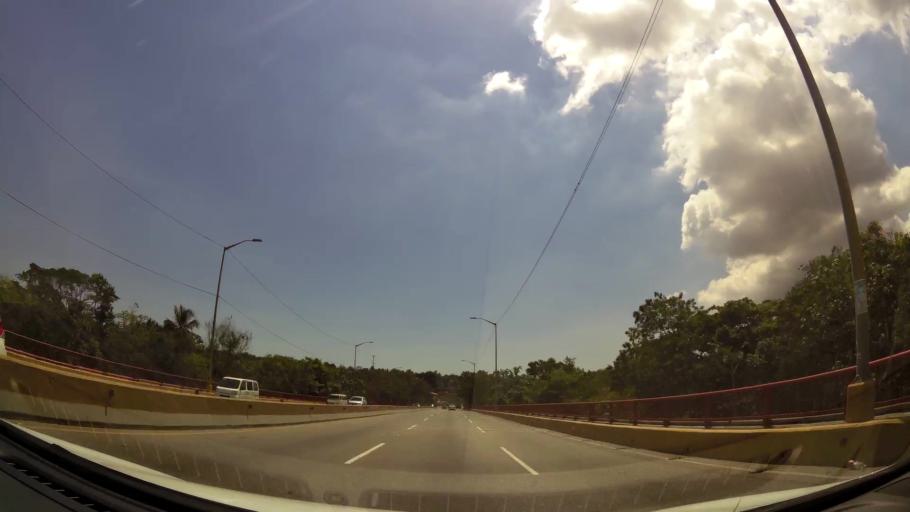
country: DO
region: Nacional
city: La Agustina
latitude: 18.5160
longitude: -69.9537
